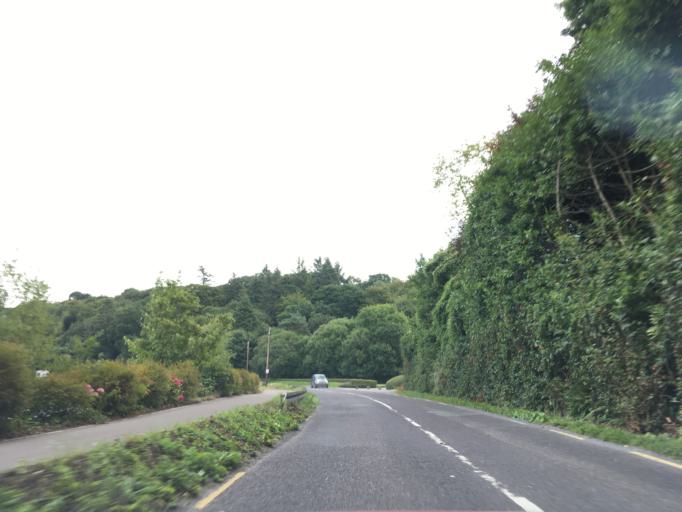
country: IE
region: Munster
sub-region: County Cork
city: Crosshaven
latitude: 51.8013
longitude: -8.3289
